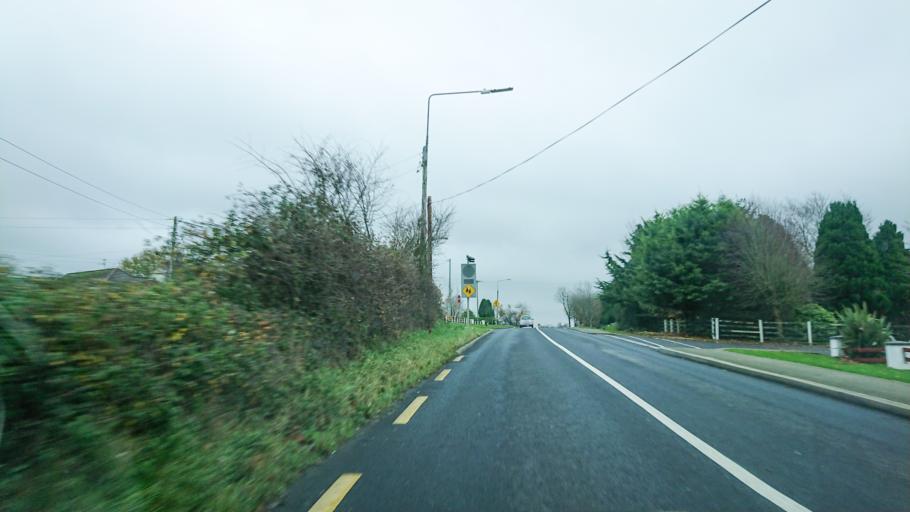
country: IE
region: Leinster
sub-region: Kilkenny
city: Mooncoin
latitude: 52.2973
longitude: -7.2636
